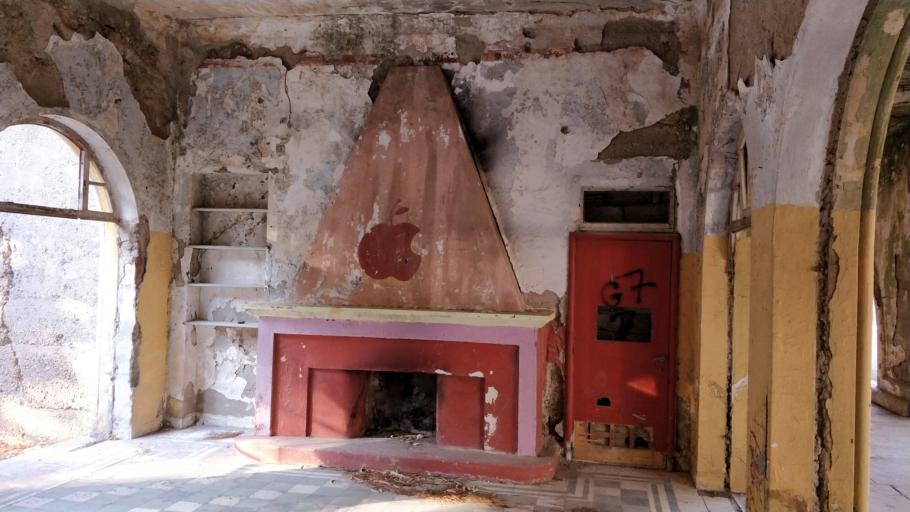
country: GR
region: South Aegean
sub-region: Nomos Dodekanisou
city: Archangelos
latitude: 36.2743
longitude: 28.0264
